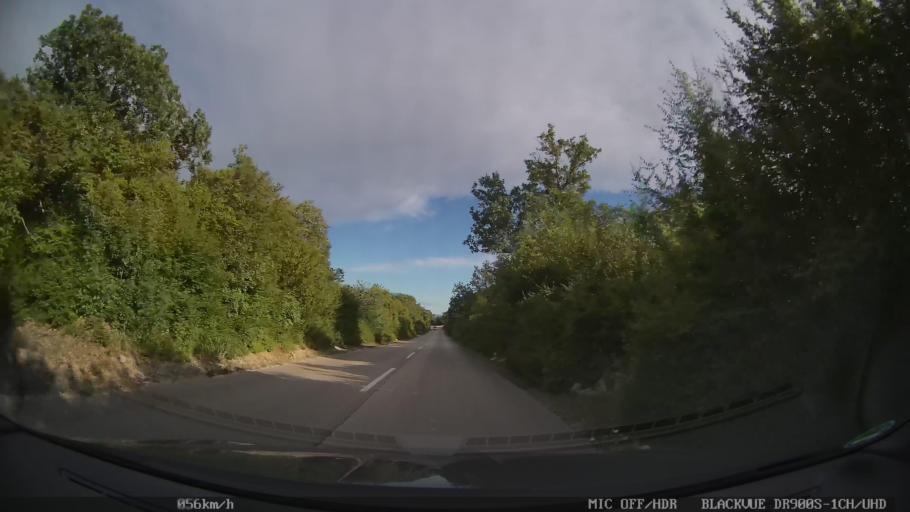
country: HR
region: Primorsko-Goranska
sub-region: Grad Krk
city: Krk
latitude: 45.0656
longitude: 14.4732
